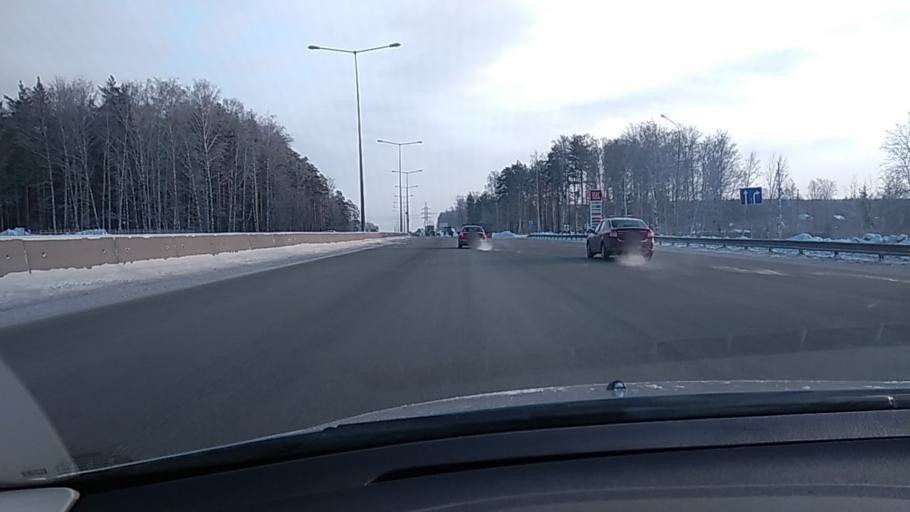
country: RU
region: Sverdlovsk
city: Istok
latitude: 56.7742
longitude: 60.7180
